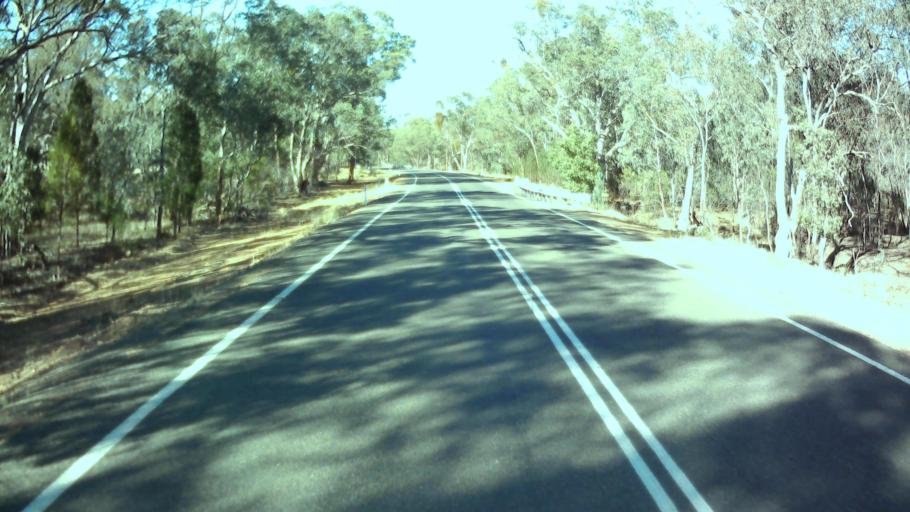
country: AU
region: New South Wales
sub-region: Weddin
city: Grenfell
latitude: -34.0019
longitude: 148.1279
